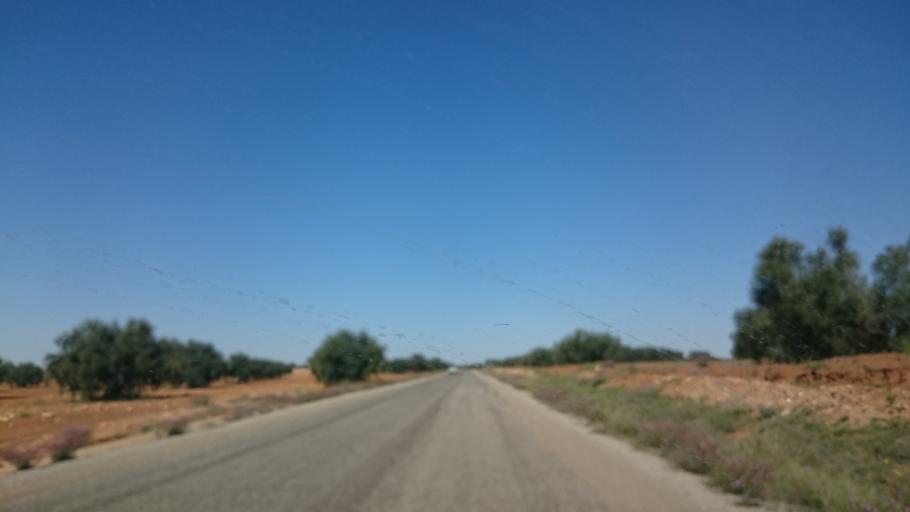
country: TN
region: Safaqis
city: Bi'r `Ali Bin Khalifah
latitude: 34.8613
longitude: 10.4195
